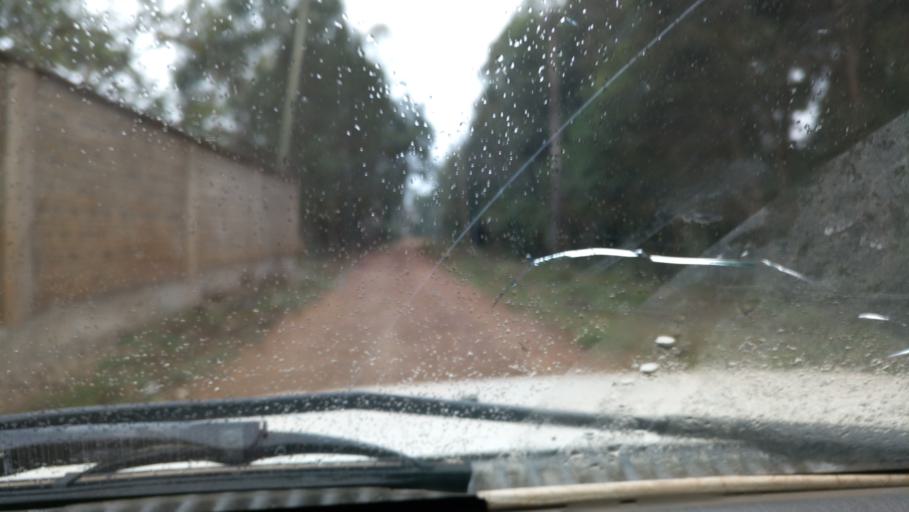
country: KE
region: Kajiado
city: Ngong
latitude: -1.3621
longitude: 36.7431
